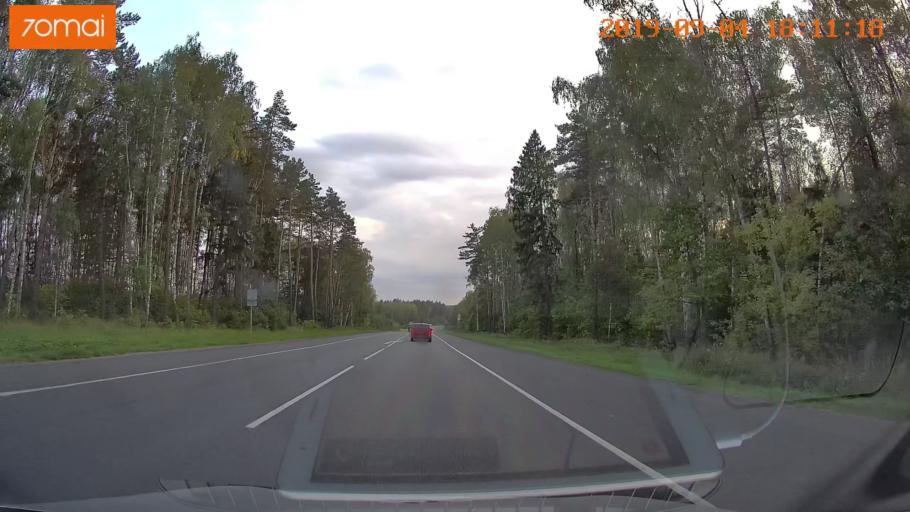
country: RU
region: Moskovskaya
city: Lopatinskiy
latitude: 55.3792
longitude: 38.7558
